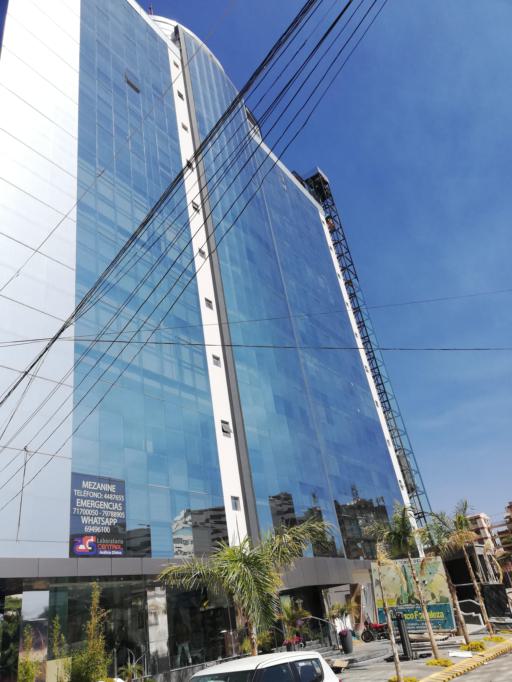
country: BO
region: Cochabamba
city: Cochabamba
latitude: -17.3850
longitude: -66.1485
